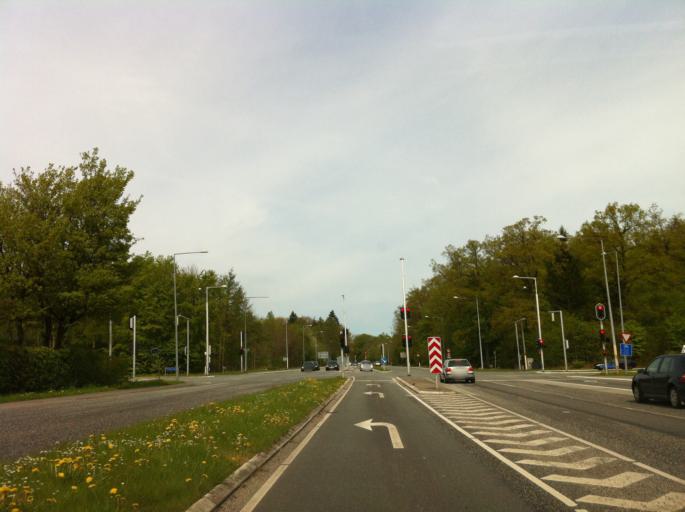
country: DK
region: Capital Region
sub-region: Hillerod Kommune
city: Hillerod
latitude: 55.9203
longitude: 12.3323
